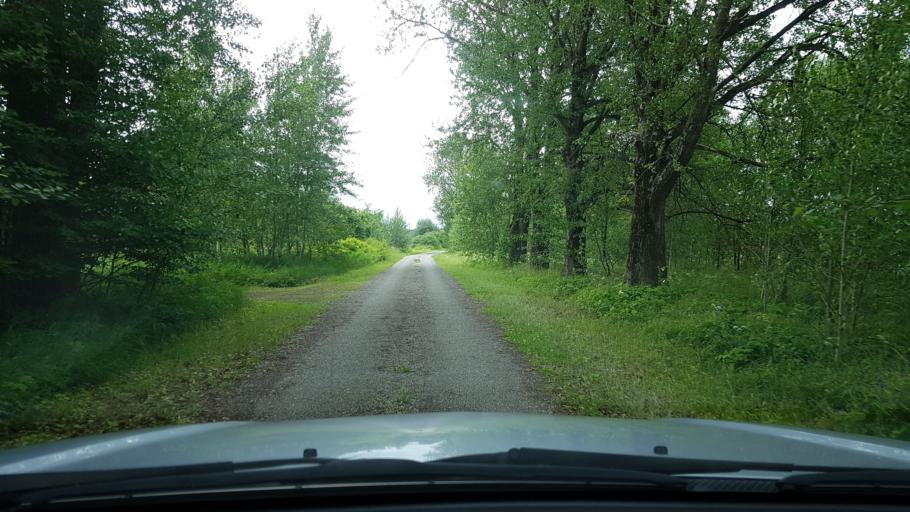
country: EE
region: Ida-Virumaa
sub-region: Narva-Joesuu linn
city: Narva-Joesuu
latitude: 59.3428
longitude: 27.9427
